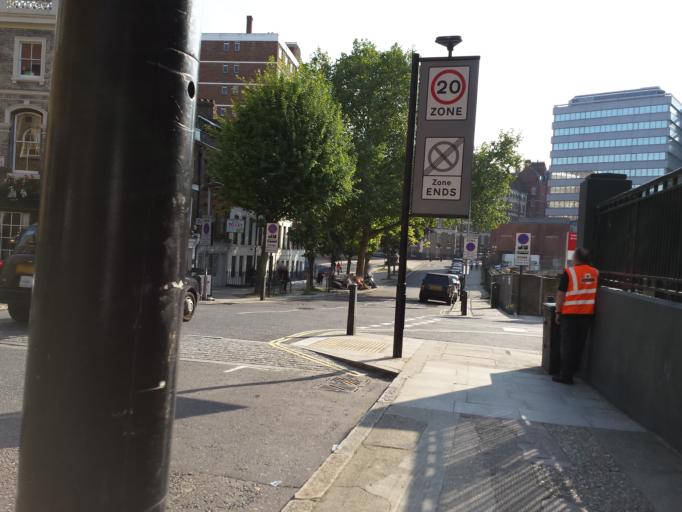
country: GB
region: England
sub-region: Greater London
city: Clerkenwell
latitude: 51.5238
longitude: -0.1120
